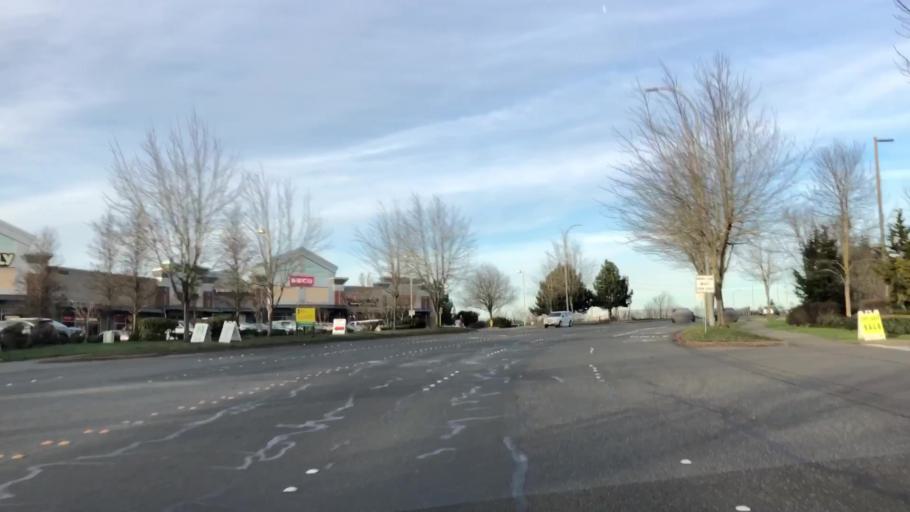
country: US
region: Washington
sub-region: Snohomish County
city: Alderwood Manor
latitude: 47.8233
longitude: -122.2710
